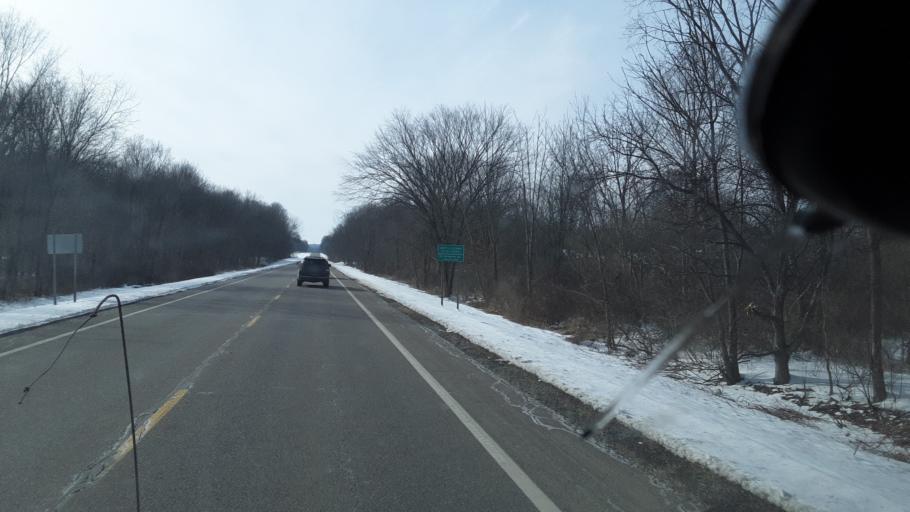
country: US
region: Ohio
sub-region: Stark County
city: Hartville
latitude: 41.0301
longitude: -81.2294
